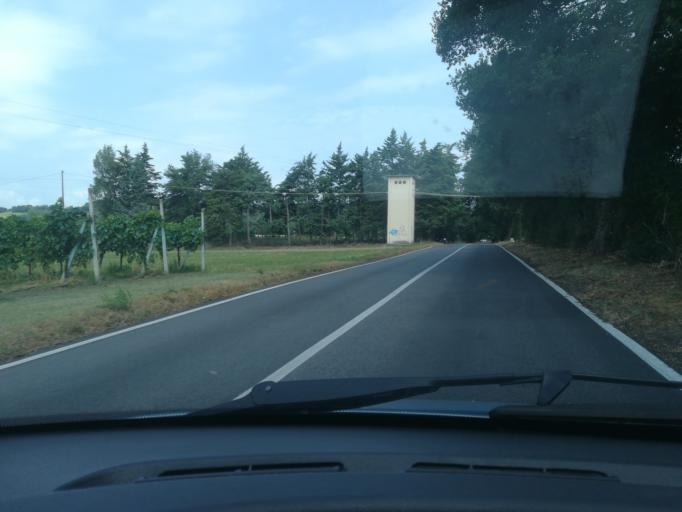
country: IT
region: The Marches
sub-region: Provincia di Macerata
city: Sforzacosta
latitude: 43.2699
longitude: 13.4373
